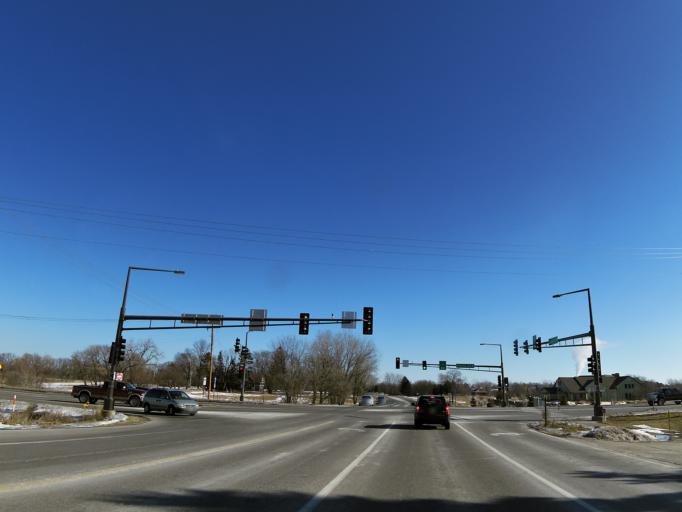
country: US
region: Minnesota
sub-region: Washington County
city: Grant
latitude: 45.0577
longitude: -92.8637
